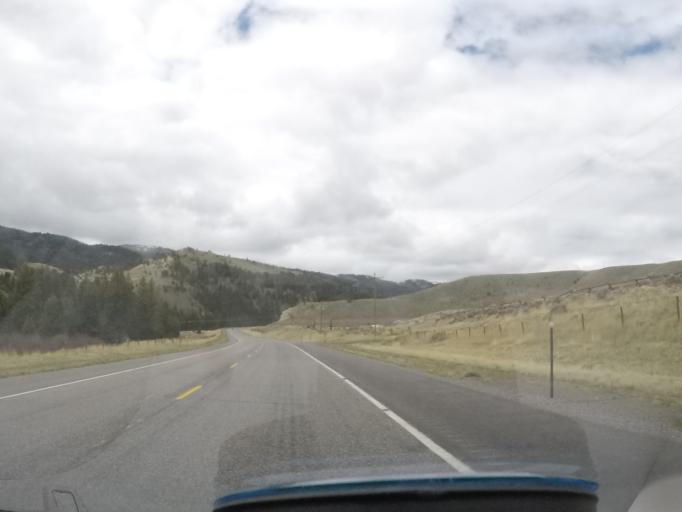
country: US
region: Wyoming
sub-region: Sublette County
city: Pinedale
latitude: 43.5793
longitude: -109.7499
